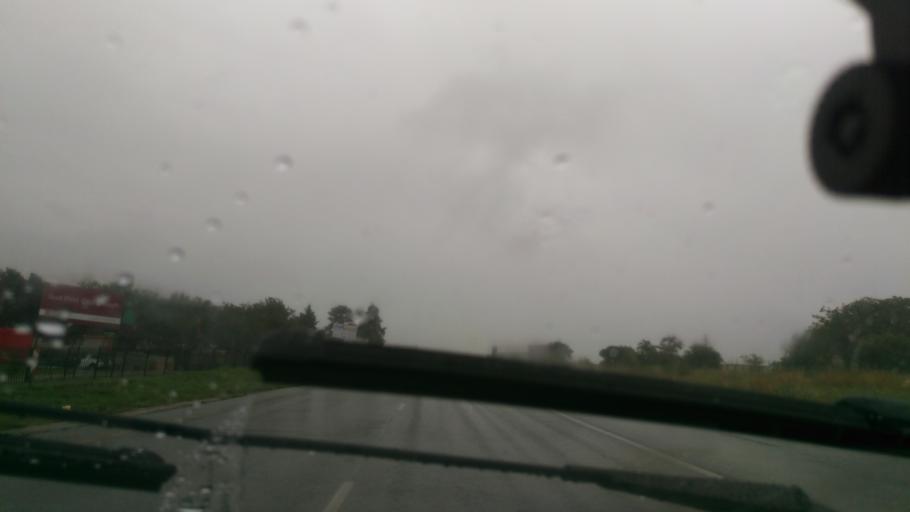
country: ZA
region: Gauteng
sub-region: City of Johannesburg Metropolitan Municipality
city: Diepsloot
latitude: -26.0304
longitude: 27.9717
